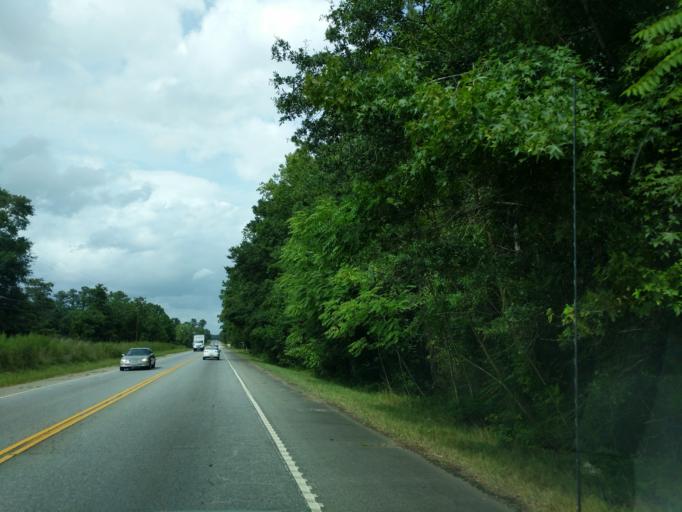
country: US
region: South Carolina
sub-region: Anderson County
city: Anderson
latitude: 34.5301
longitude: -82.5874
